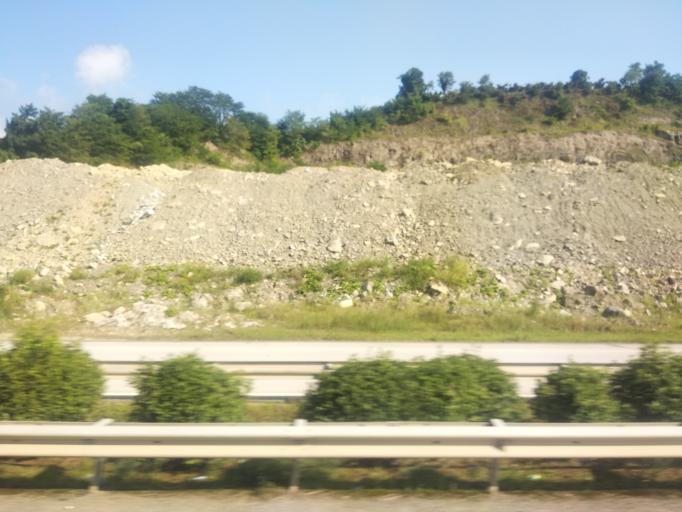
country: TR
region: Ordu
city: Ordu
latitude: 40.9983
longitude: 37.8209
